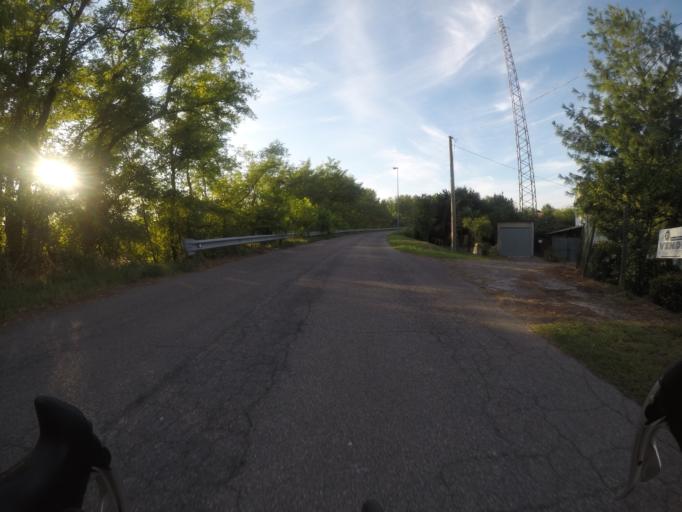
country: IT
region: Veneto
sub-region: Provincia di Rovigo
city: Castelguglielmo
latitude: 45.0055
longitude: 11.5636
